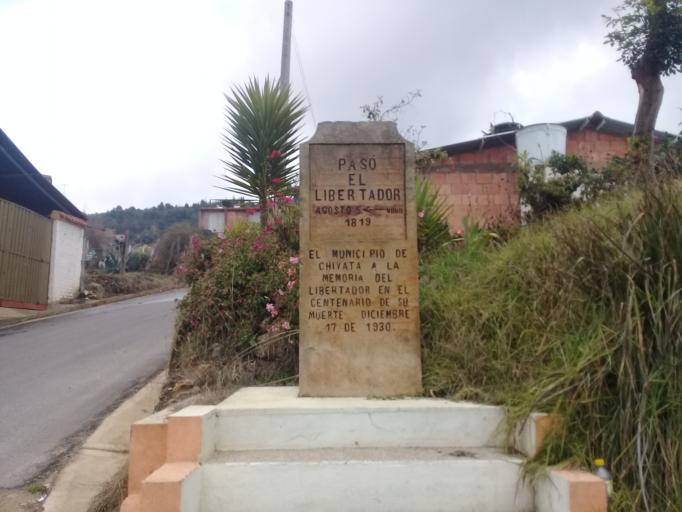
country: CO
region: Boyaca
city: Siachoque
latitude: 5.5565
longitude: -73.2840
